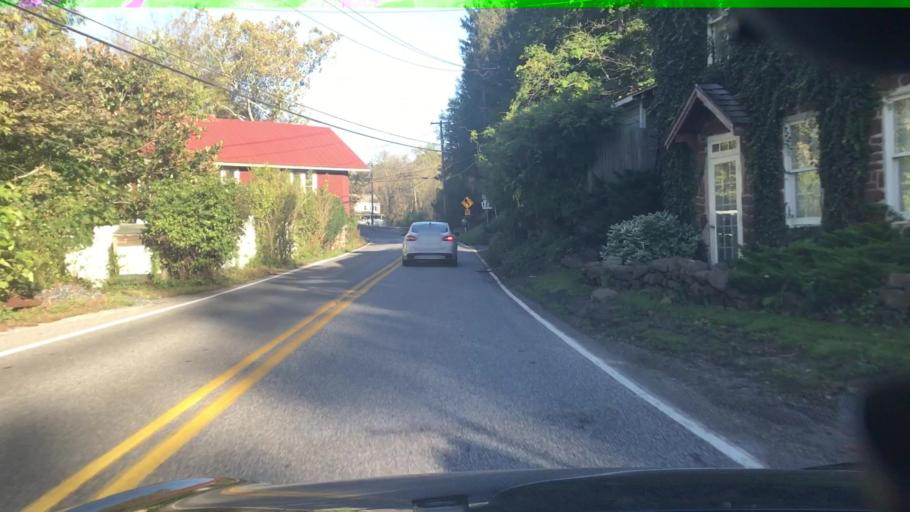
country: US
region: Pennsylvania
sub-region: Cumberland County
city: Lower Allen
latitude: 40.1677
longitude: -76.9050
